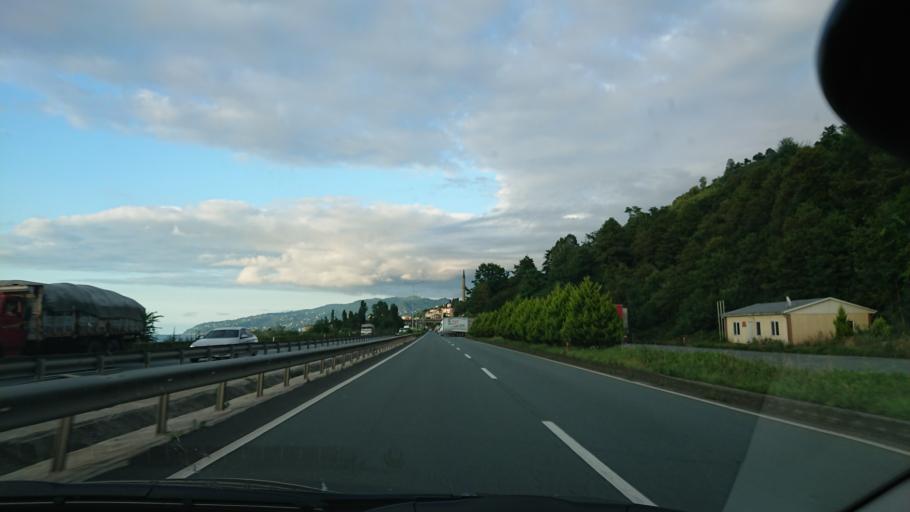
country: TR
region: Rize
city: Buyukkoy
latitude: 41.0706
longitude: 40.6603
